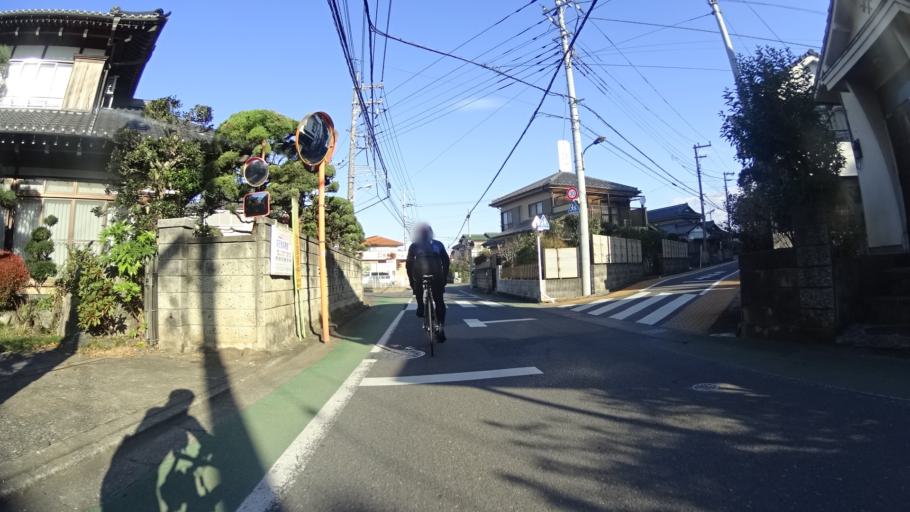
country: JP
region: Tokyo
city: Fussa
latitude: 35.7764
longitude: 139.3497
